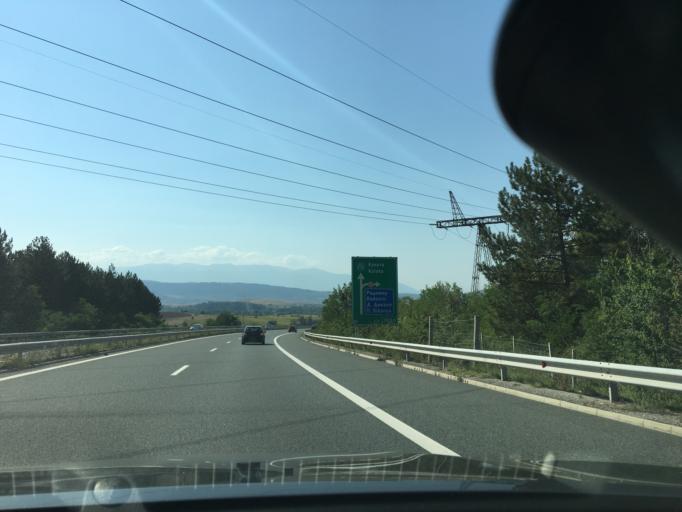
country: BG
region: Kyustendil
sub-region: Obshtina Bobovdol
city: Bobovdol
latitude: 42.4625
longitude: 23.1127
